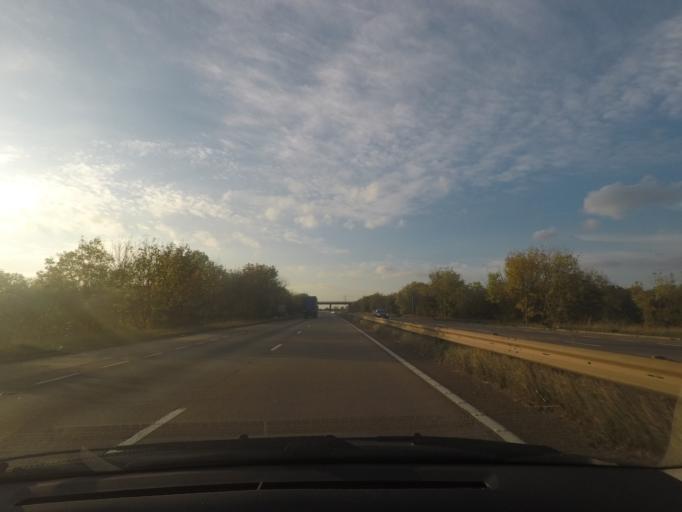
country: GB
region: England
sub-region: North East Lincolnshire
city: Healing
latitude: 53.5930
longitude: -0.1708
